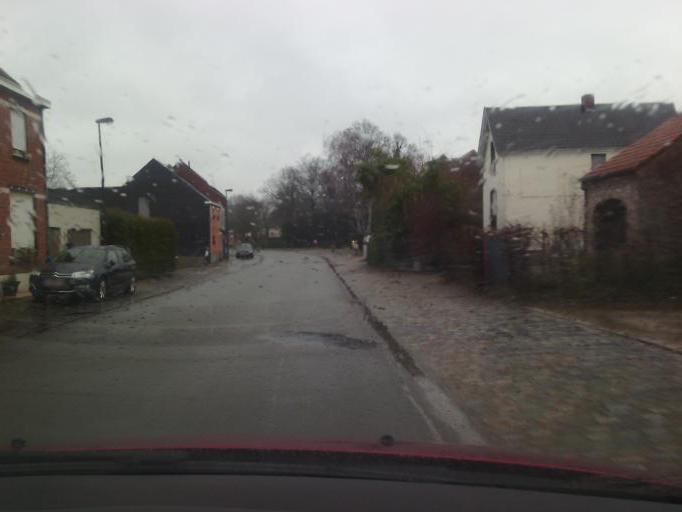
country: BE
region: Flanders
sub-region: Provincie Oost-Vlaanderen
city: Berlare
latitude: 51.0226
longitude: 3.9949
